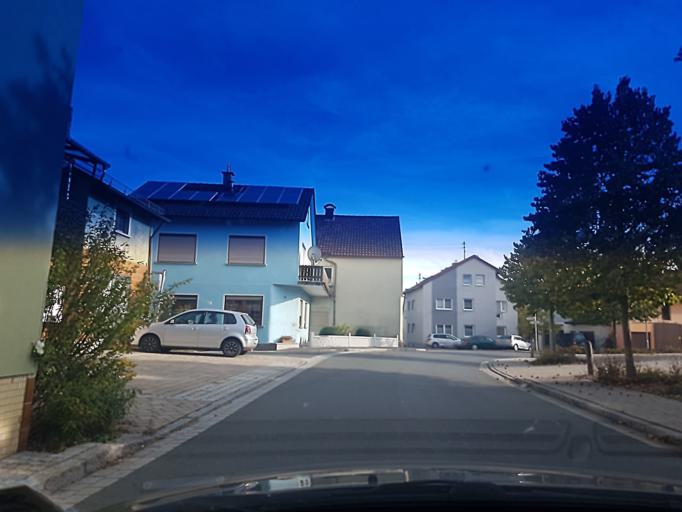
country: DE
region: Bavaria
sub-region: Regierungsbezirk Mittelfranken
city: Burghaslach
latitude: 49.7722
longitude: 10.5625
